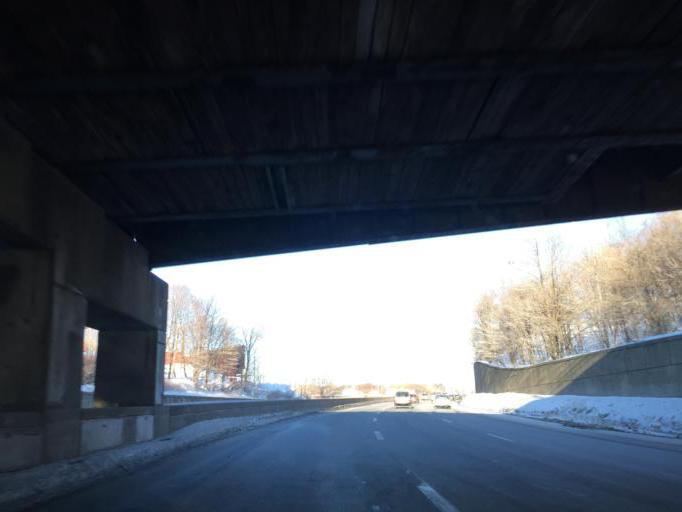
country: US
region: Massachusetts
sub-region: Suffolk County
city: Chelsea
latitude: 42.4025
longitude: -71.0364
